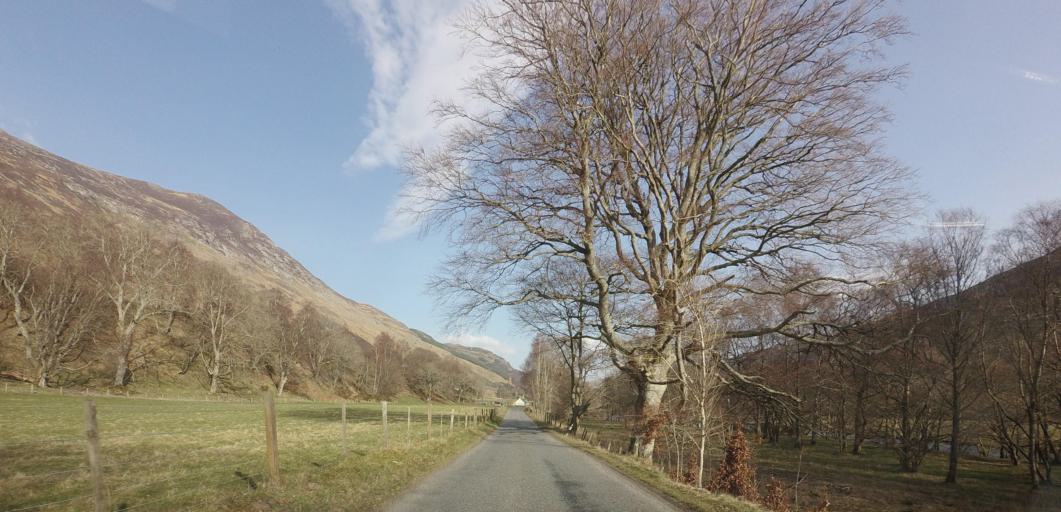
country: GB
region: Scotland
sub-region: Perth and Kinross
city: Comrie
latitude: 56.6027
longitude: -4.1513
